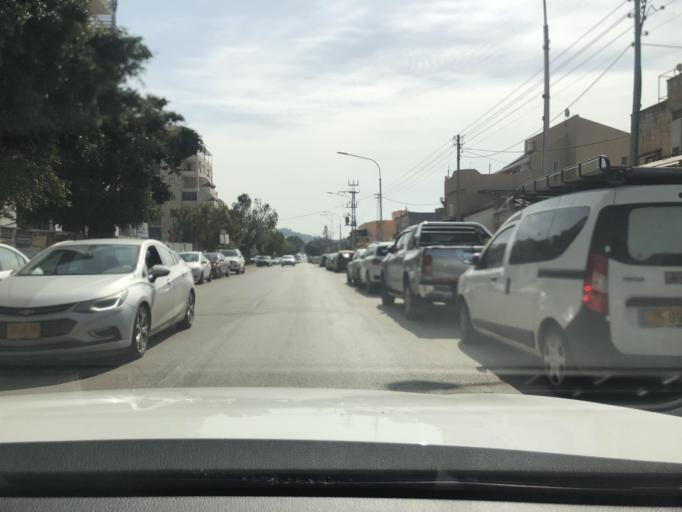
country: IL
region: Central District
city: Rosh Ha'Ayin
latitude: 32.0944
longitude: 34.9453
